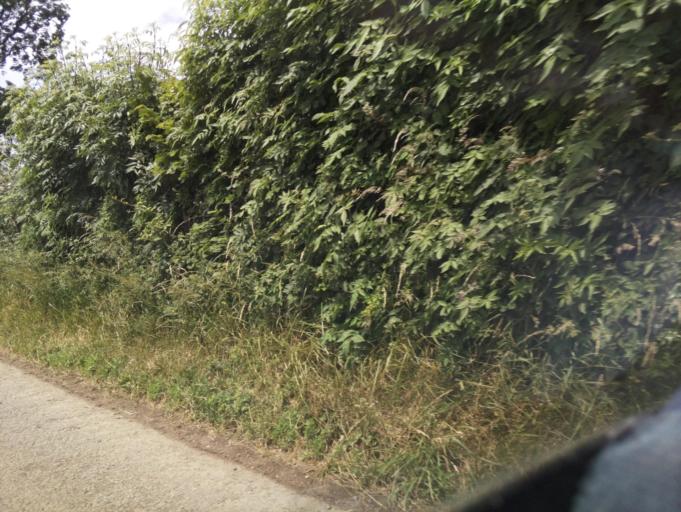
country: GB
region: Wales
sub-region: Vale of Glamorgan
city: Penllyn
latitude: 51.4706
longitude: -3.4859
